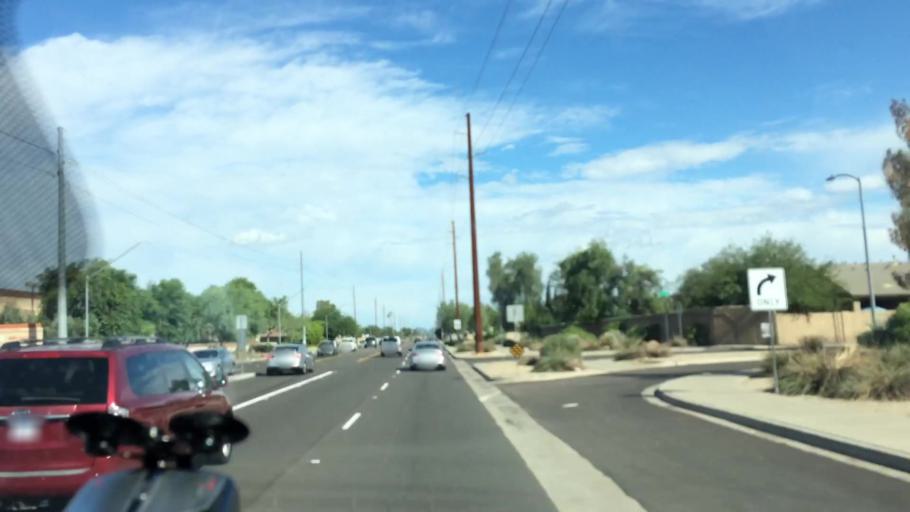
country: US
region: Arizona
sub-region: Maricopa County
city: Glendale
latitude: 33.5673
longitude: -112.1846
